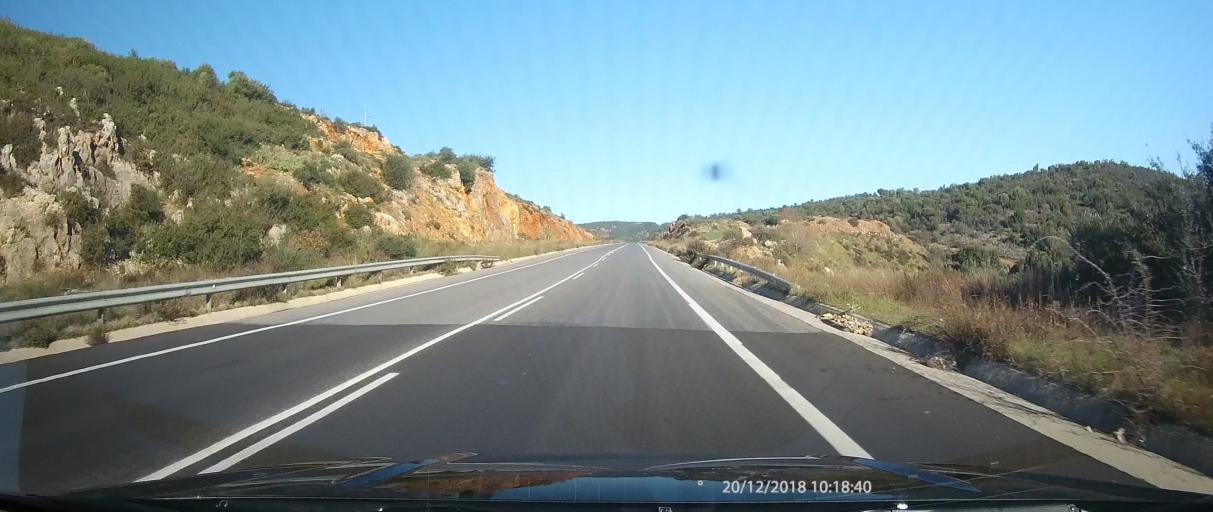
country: GR
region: Peloponnese
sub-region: Nomos Lakonias
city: Magoula
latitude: 37.1205
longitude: 22.4210
